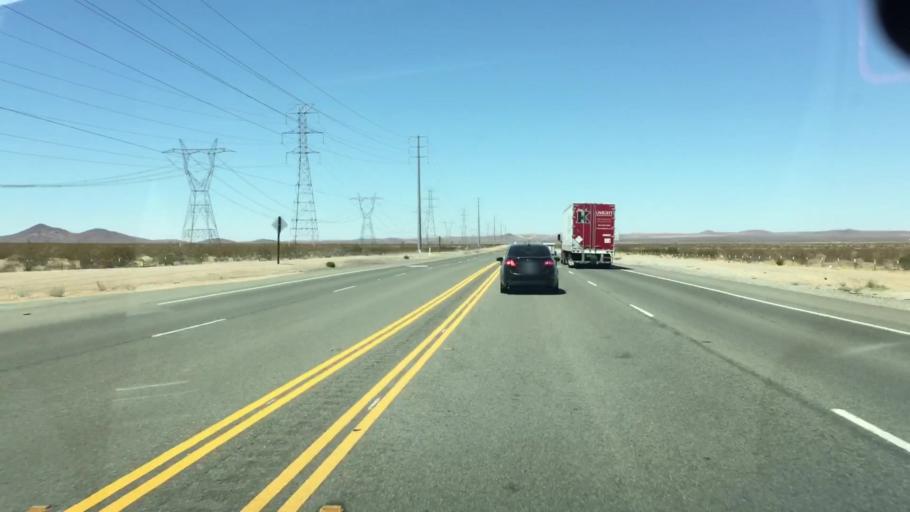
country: US
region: California
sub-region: San Bernardino County
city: Adelanto
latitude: 34.7627
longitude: -117.4747
